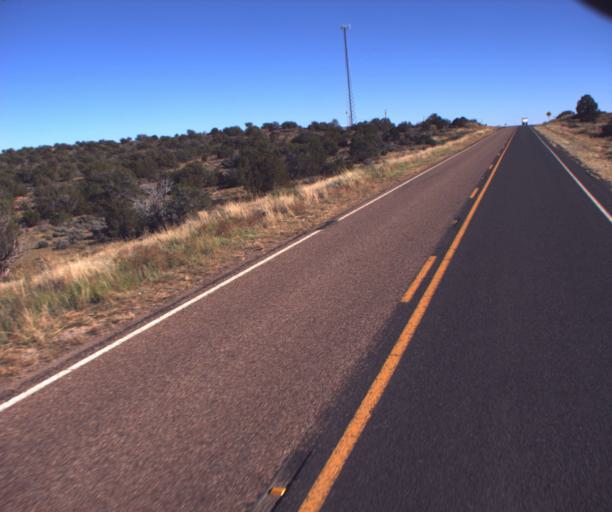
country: US
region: Arizona
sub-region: Apache County
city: Houck
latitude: 35.3501
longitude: -109.4560
